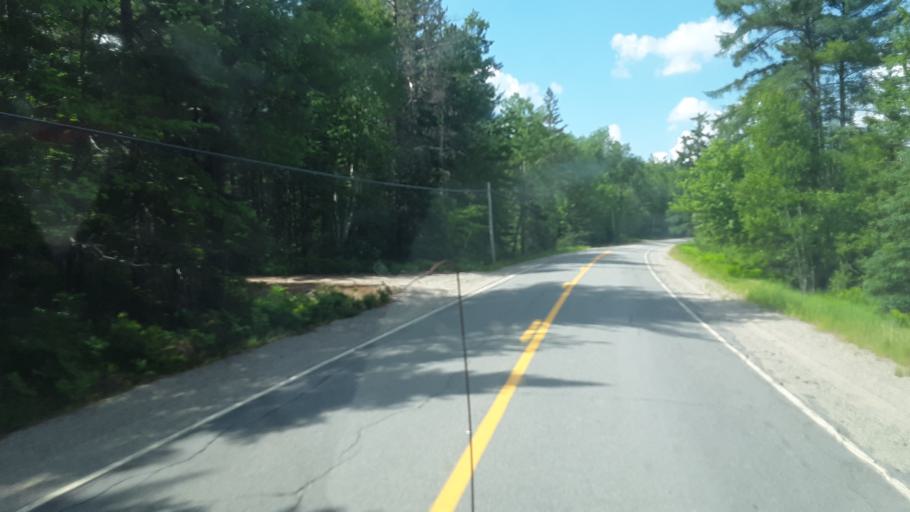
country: US
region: Maine
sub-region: Washington County
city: Machias
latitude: 44.8802
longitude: -67.6216
